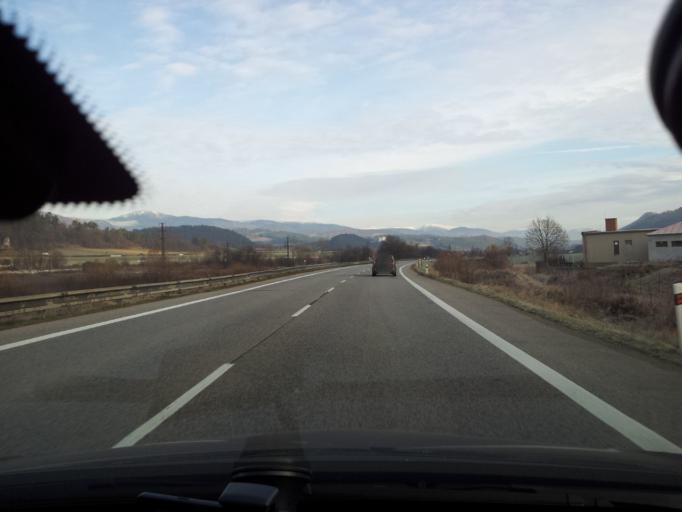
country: SK
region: Banskobystricky
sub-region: Okres Banska Bystrica
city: Banska Bystrica
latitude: 48.7536
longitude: 19.2572
